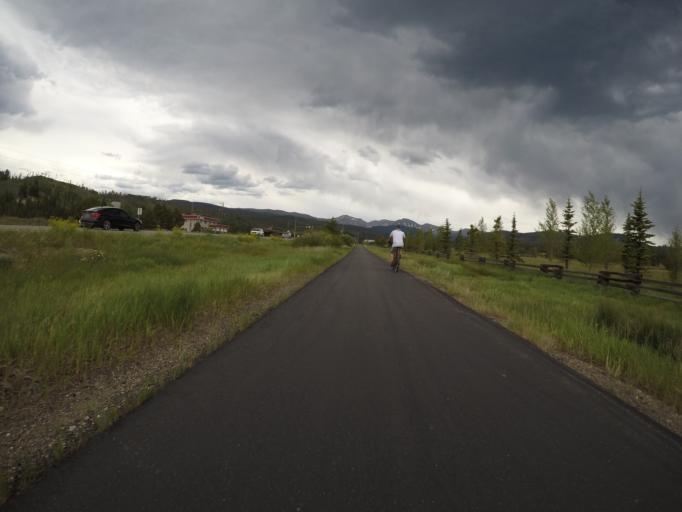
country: US
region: Colorado
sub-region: Grand County
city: Fraser
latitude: 39.9353
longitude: -105.7954
